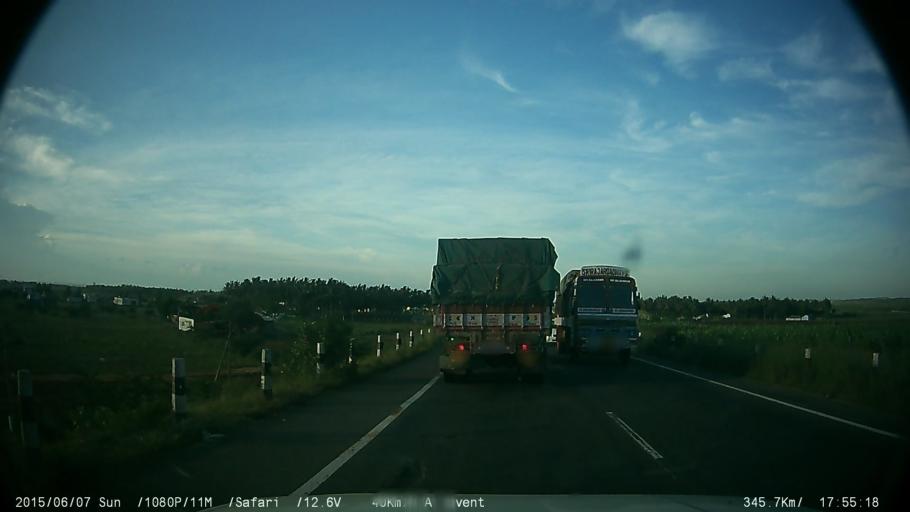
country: IN
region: Tamil Nadu
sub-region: Coimbatore
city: Chettipalaiyam
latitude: 10.9449
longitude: 77.0125
